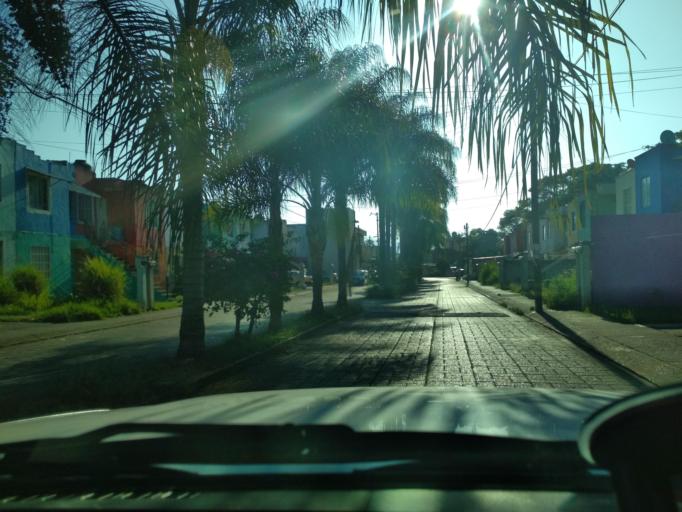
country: MX
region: Veracruz
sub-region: Fortin
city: Fraccionamiento Villas de la Llave
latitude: 18.9188
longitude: -96.9917
